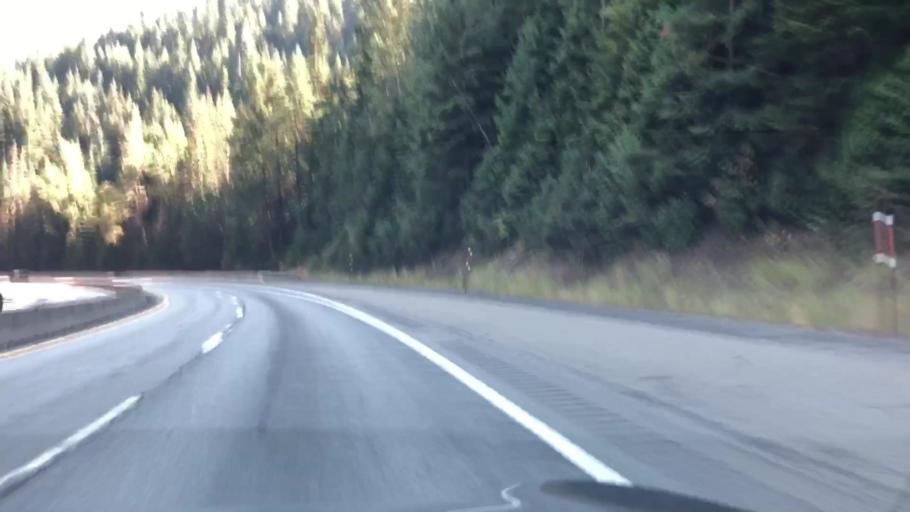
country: US
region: Idaho
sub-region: Kootenai County
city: Coeur d'Alene
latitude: 47.6073
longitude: -116.5113
